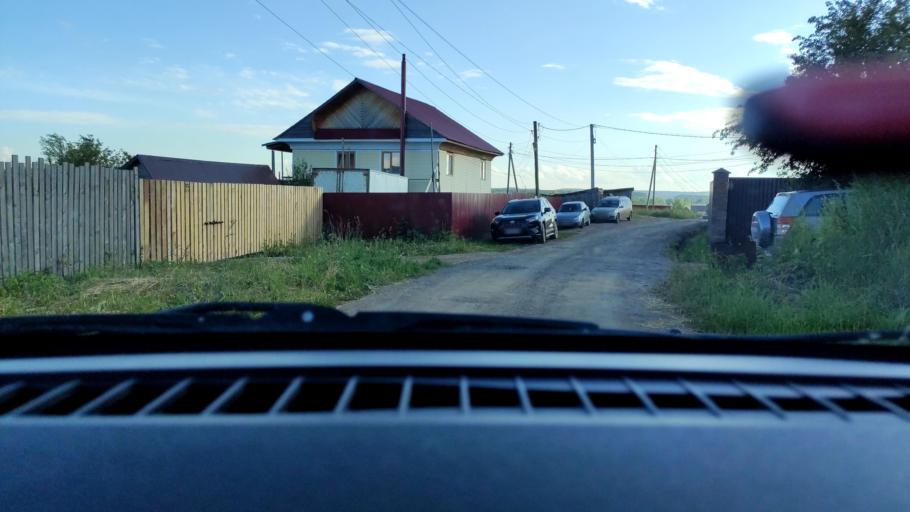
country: RU
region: Perm
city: Kultayevo
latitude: 57.9019
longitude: 55.9286
